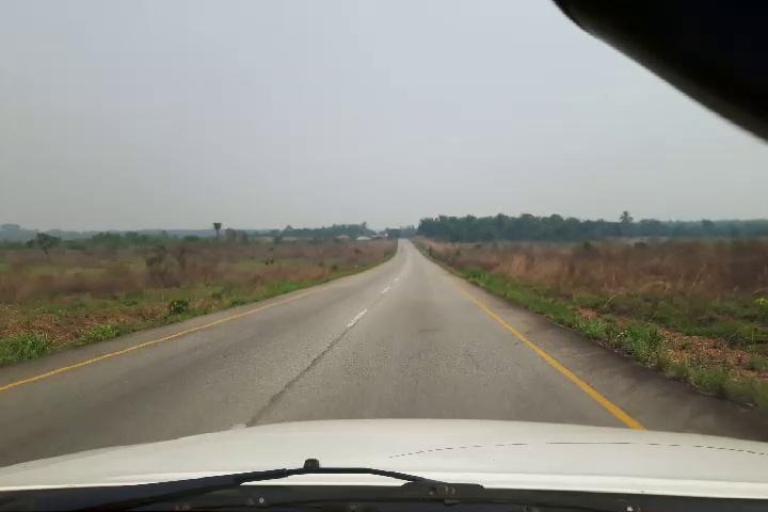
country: SL
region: Southern Province
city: Largo
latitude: 8.2248
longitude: -12.0759
